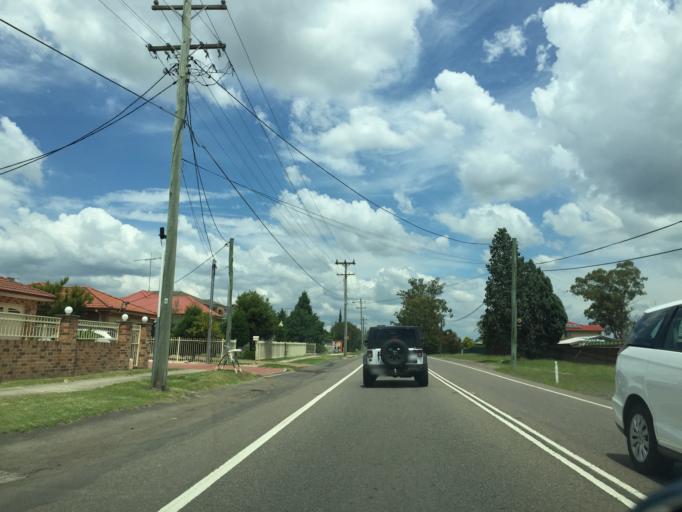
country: AU
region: New South Wales
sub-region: Blacktown
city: Hassall Grove
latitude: -33.7412
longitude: 150.8433
